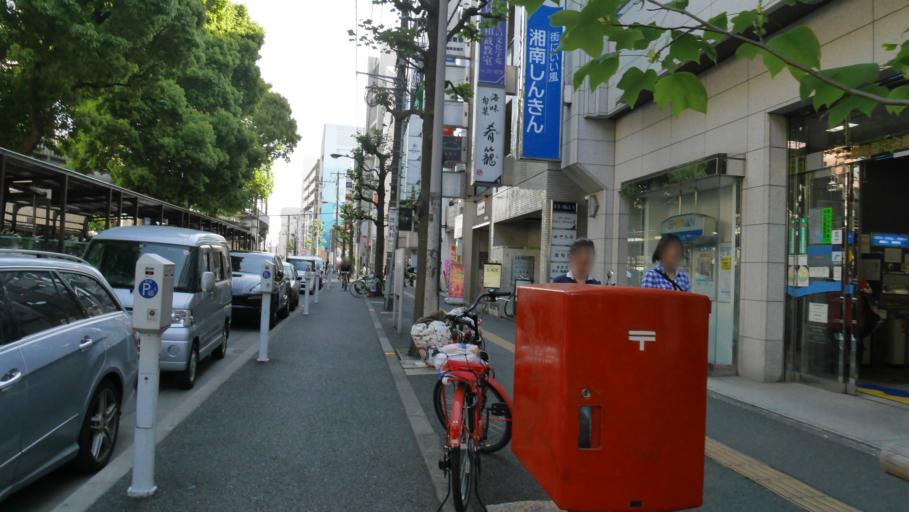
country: JP
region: Kanagawa
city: Fujisawa
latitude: 35.3368
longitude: 139.4867
